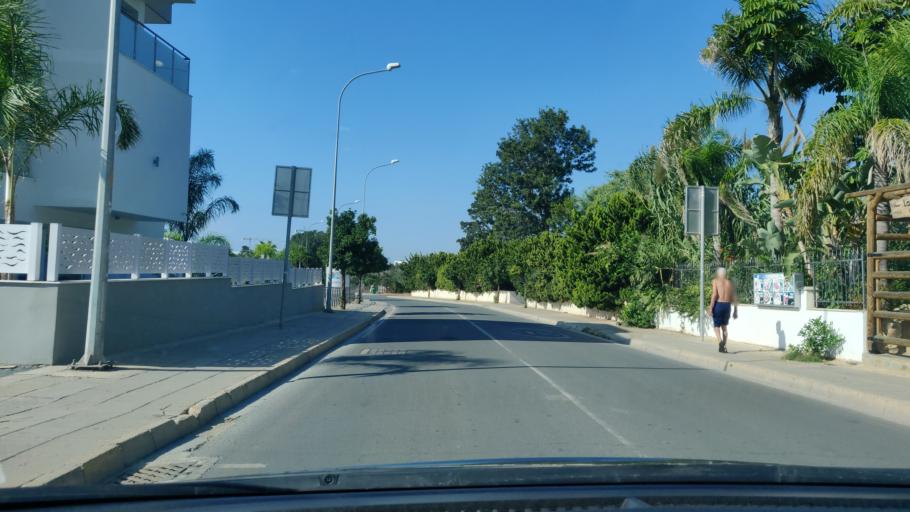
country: CY
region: Ammochostos
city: Ayia Napa
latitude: 34.9900
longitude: 33.9897
